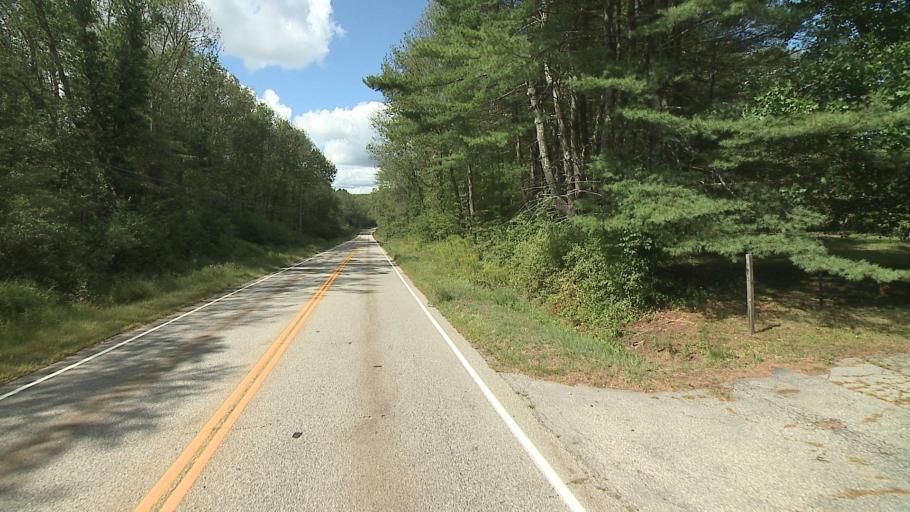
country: US
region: Connecticut
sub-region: Windham County
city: South Woodstock
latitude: 41.8595
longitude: -72.0324
